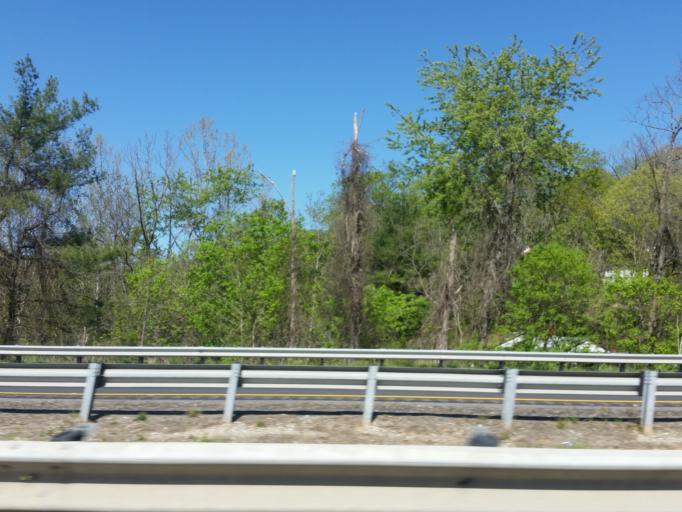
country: US
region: North Carolina
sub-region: Buncombe County
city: Woodfin
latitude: 35.6233
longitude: -82.5758
